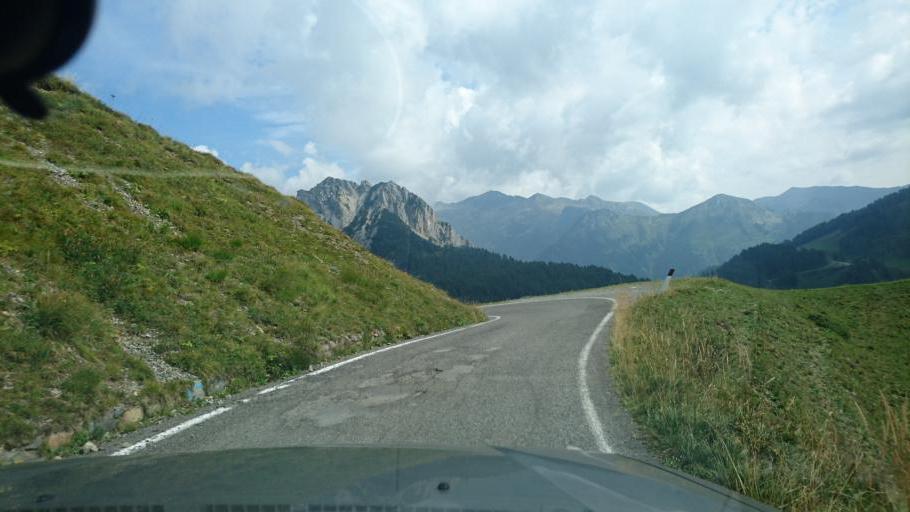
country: IT
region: Lombardy
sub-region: Provincia di Brescia
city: Bagolino
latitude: 45.9128
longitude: 10.4242
